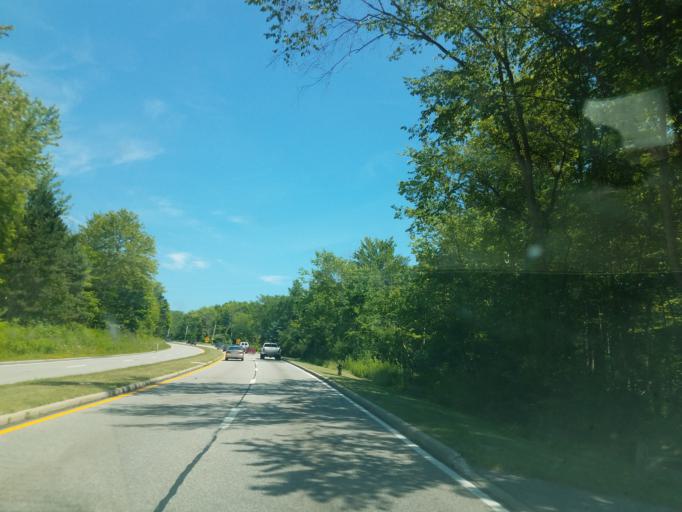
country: US
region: Ohio
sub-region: Cuyahoga County
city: Gates Mills
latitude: 41.5231
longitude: -81.3952
